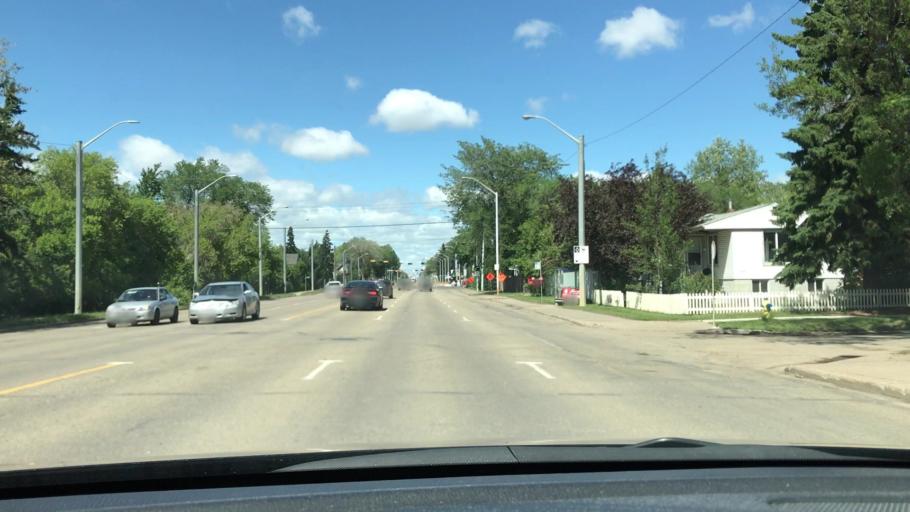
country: CA
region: Alberta
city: Edmonton
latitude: 53.5101
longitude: -113.5121
